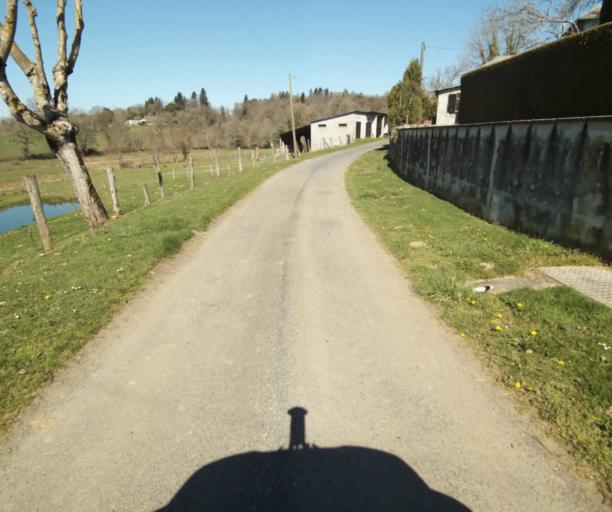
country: FR
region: Limousin
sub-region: Departement de la Correze
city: Saint-Clement
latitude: 45.3382
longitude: 1.6423
